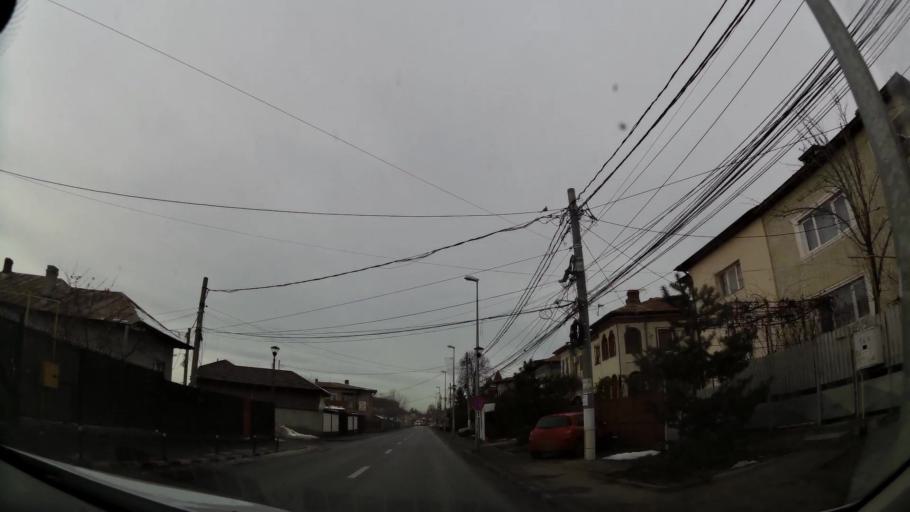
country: RO
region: Ilfov
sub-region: Comuna Pantelimon
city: Pantelimon
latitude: 44.4507
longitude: 26.2080
